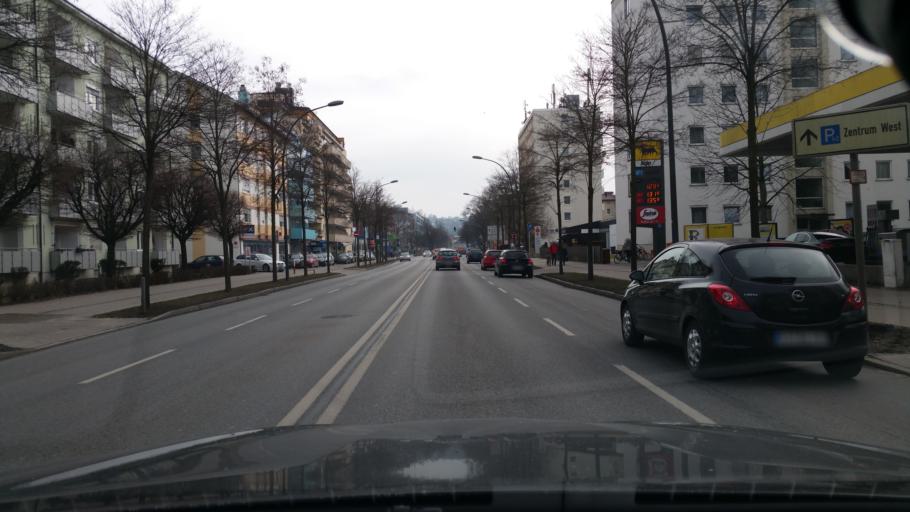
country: DE
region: Bavaria
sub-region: Lower Bavaria
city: Landshut
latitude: 48.5423
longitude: 12.1396
